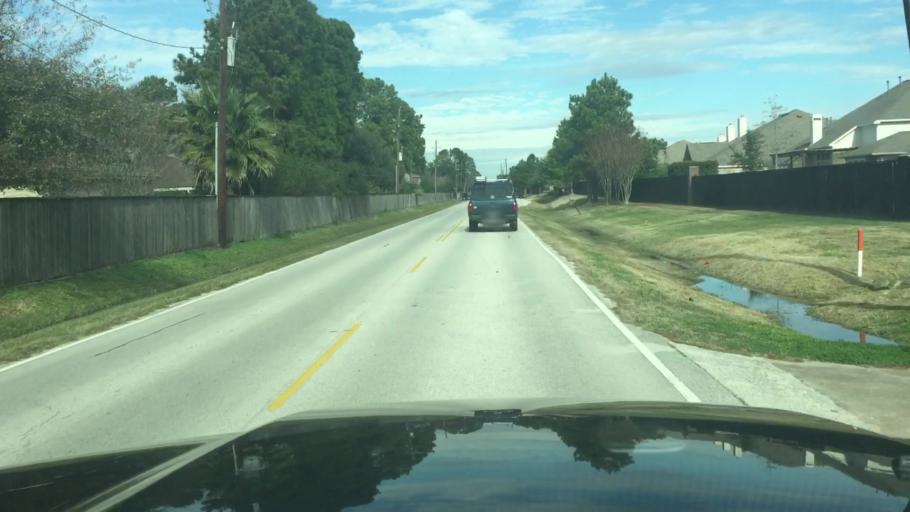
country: US
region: Texas
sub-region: Harris County
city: Oak Cliff Place
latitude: 29.8357
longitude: -95.6751
